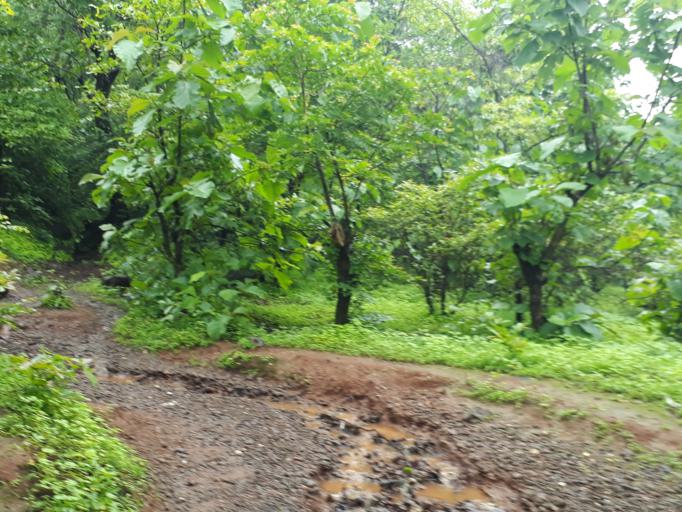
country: IN
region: Maharashtra
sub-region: Raigarh
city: Khopoli
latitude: 18.8435
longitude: 73.3800
